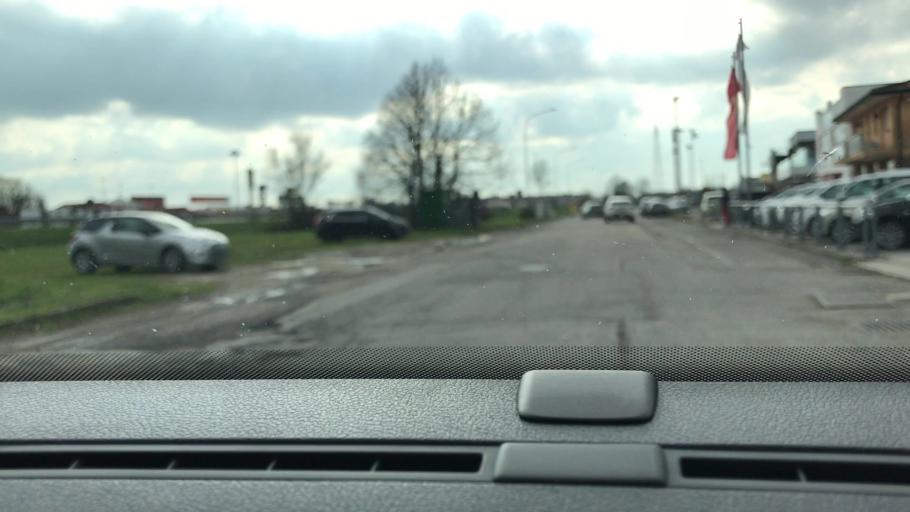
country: IT
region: Veneto
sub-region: Provincia di Rovigo
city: Grignano Polesine
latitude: 45.0351
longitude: 11.7785
